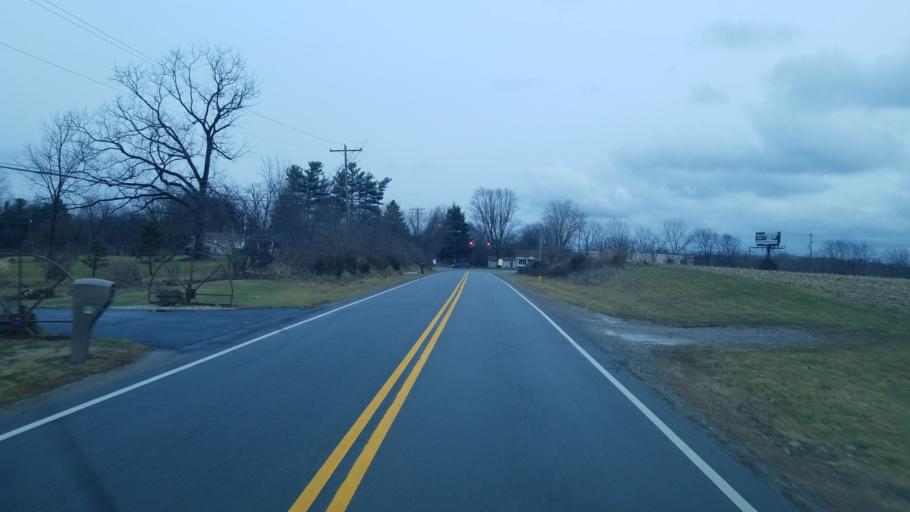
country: US
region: Ohio
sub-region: Delaware County
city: Delaware
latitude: 40.3499
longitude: -83.0761
